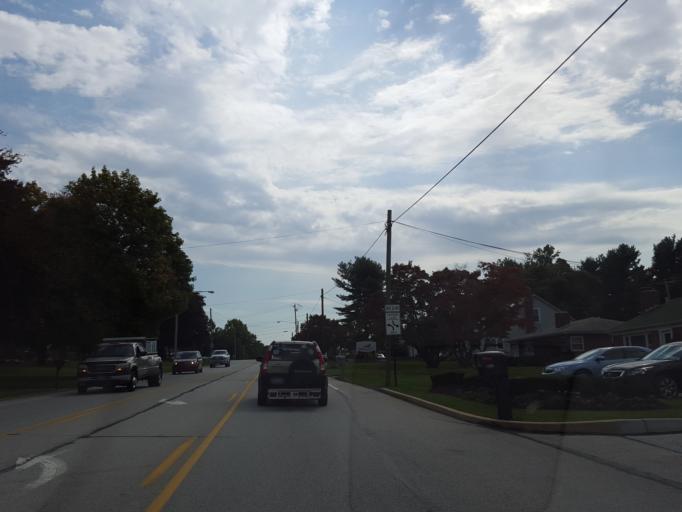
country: US
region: Pennsylvania
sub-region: York County
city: Spry
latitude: 39.9294
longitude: -76.6871
